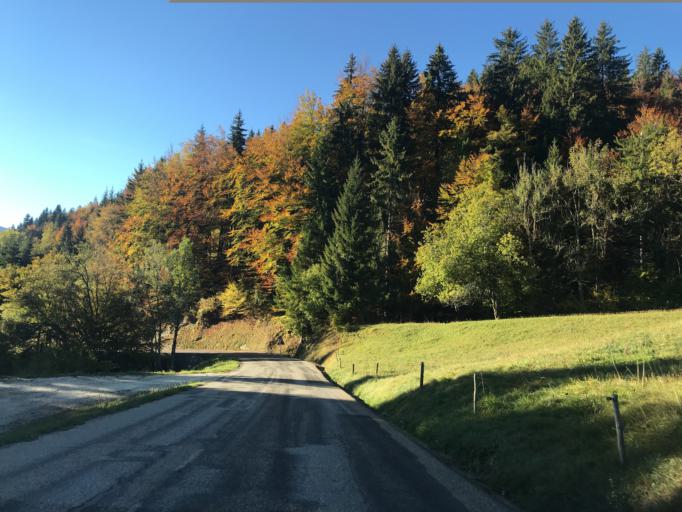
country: FR
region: Rhone-Alpes
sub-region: Departement de la Savoie
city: Vimines
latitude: 45.4586
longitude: 5.8650
